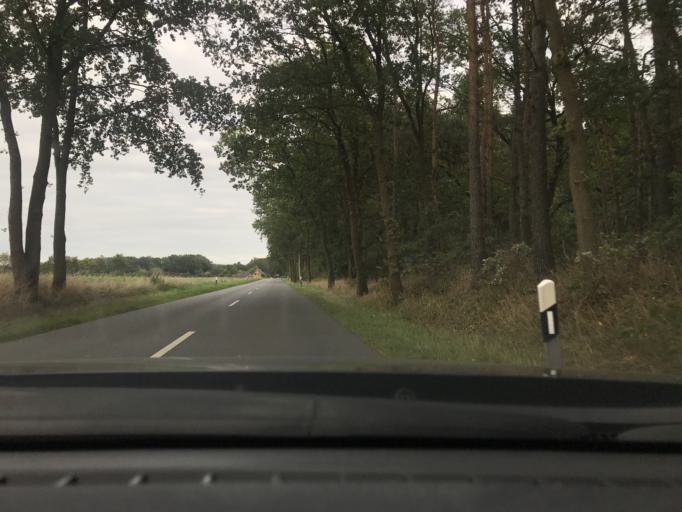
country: DE
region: Lower Saxony
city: Suderburg
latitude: 52.9129
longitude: 10.4490
